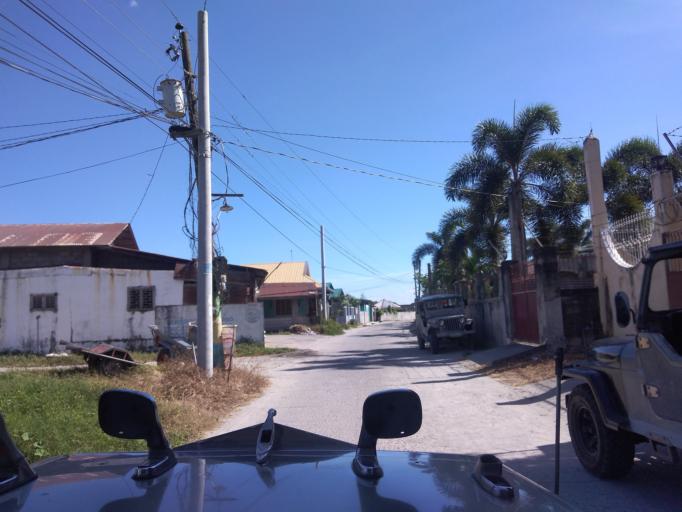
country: PH
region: Central Luzon
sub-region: Province of Pampanga
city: San Agustin
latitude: 14.9911
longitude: 120.6000
